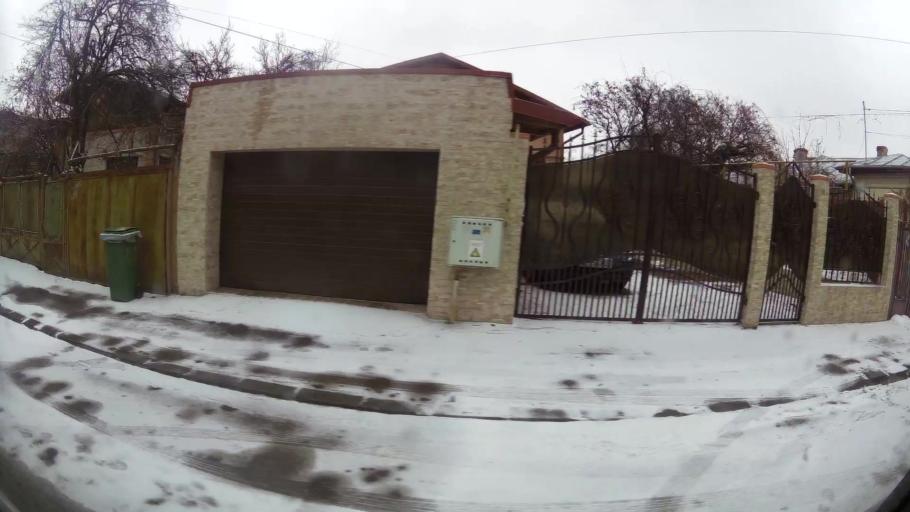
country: RO
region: Prahova
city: Ploiesti
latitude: 44.9483
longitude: 26.0225
